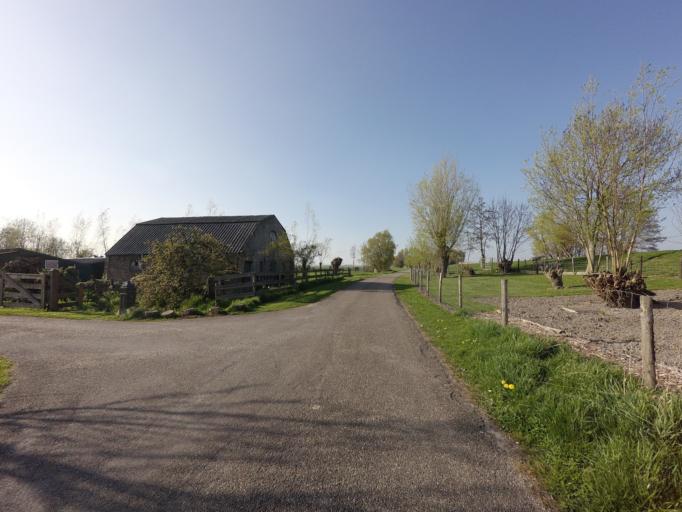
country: NL
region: South Holland
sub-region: Gemeente Vlaardingen
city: Vlaardingen
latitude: 51.9480
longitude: 4.3193
